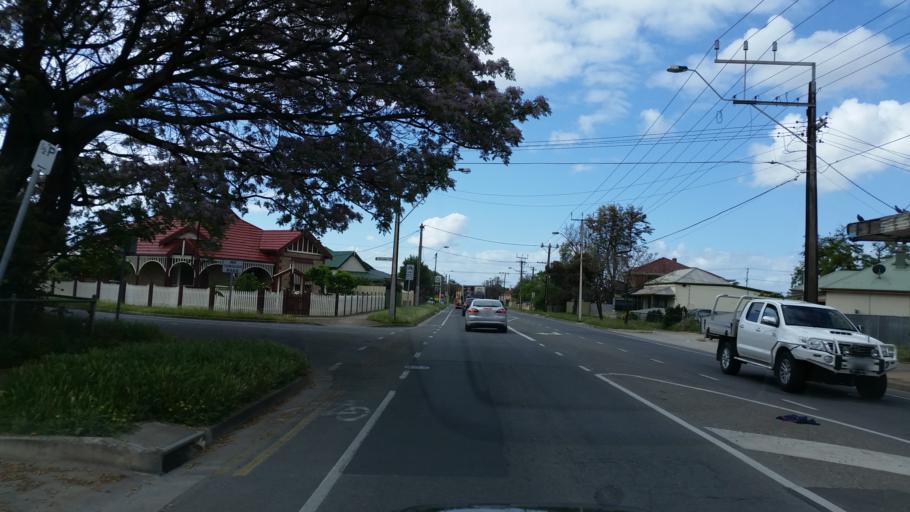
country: AU
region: South Australia
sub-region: Charles Sturt
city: Woodville
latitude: -34.8830
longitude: 138.5495
